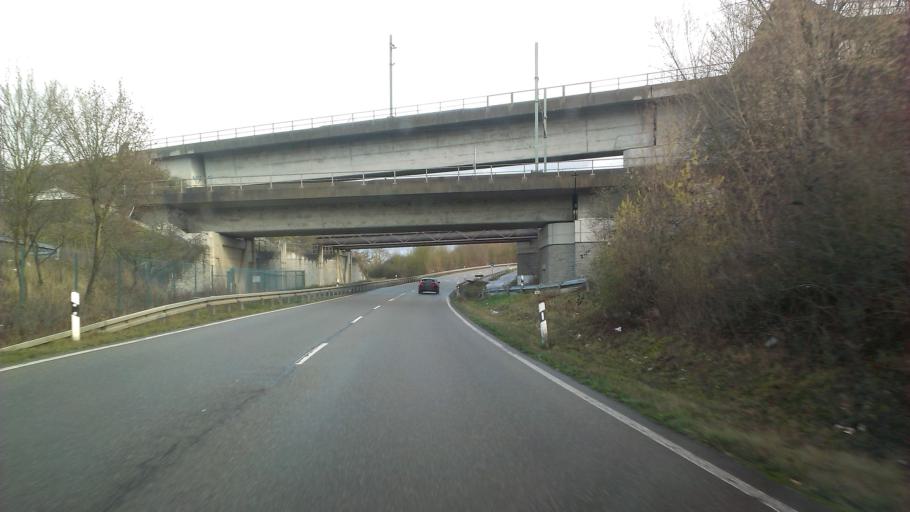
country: DE
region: Baden-Wuerttemberg
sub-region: Karlsruhe Region
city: Ubstadt-Weiher
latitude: 49.1488
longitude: 8.6170
